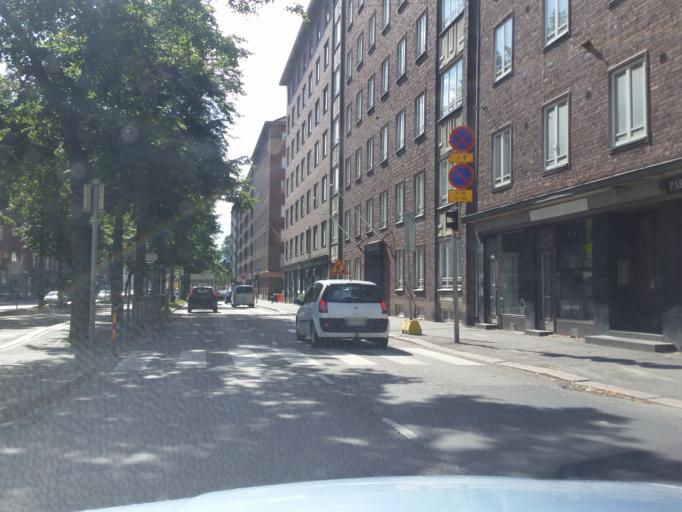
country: FI
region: Uusimaa
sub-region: Helsinki
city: Helsinki
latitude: 60.1736
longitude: 24.9191
